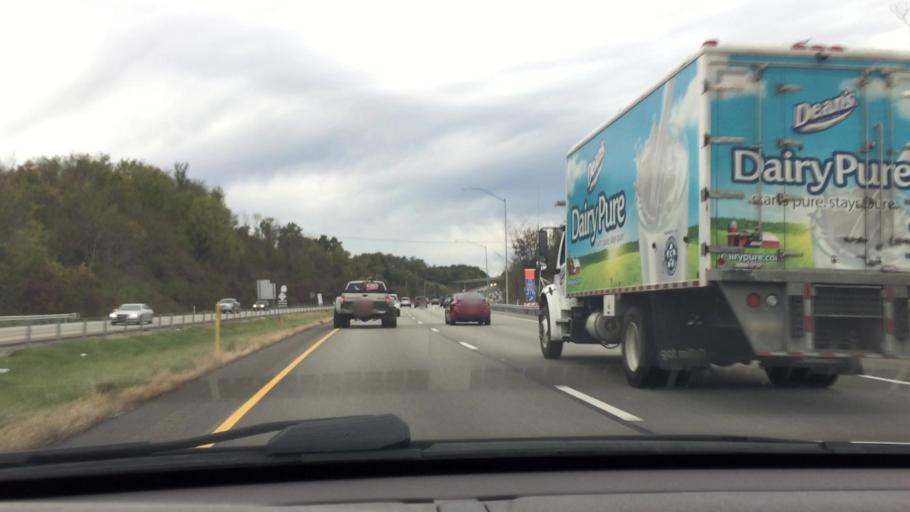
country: US
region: Pennsylvania
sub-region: Beaver County
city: Ambridge
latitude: 40.5538
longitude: -80.2783
